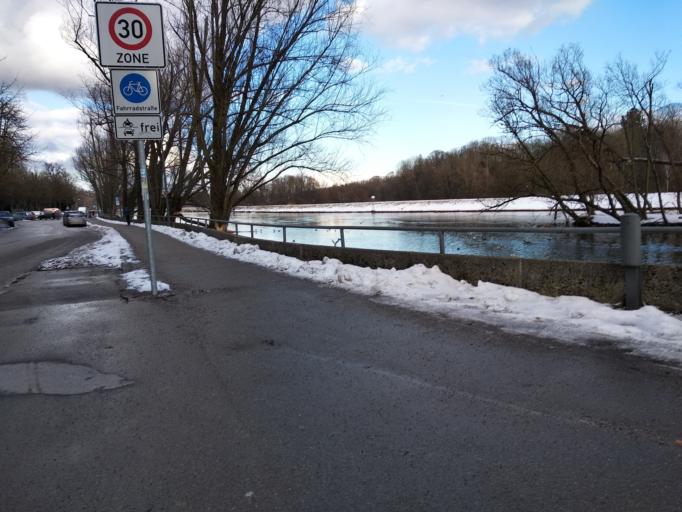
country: DE
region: Bavaria
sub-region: Upper Bavaria
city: Munich
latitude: 48.1015
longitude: 11.5480
